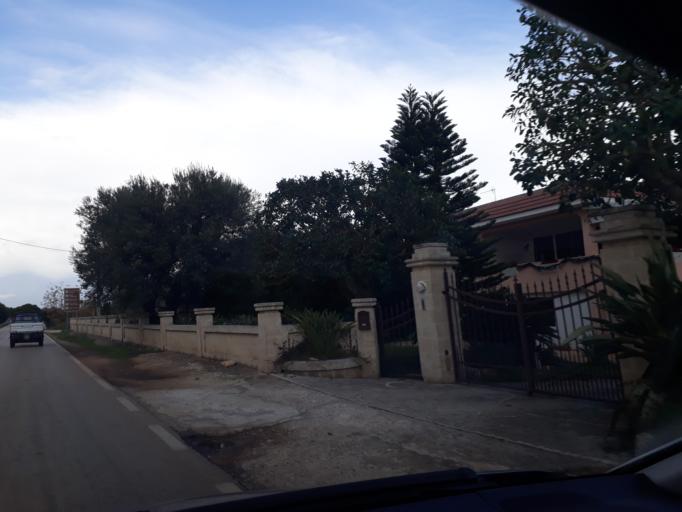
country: IT
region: Apulia
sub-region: Provincia di Brindisi
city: Fasano
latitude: 40.8225
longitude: 17.3740
